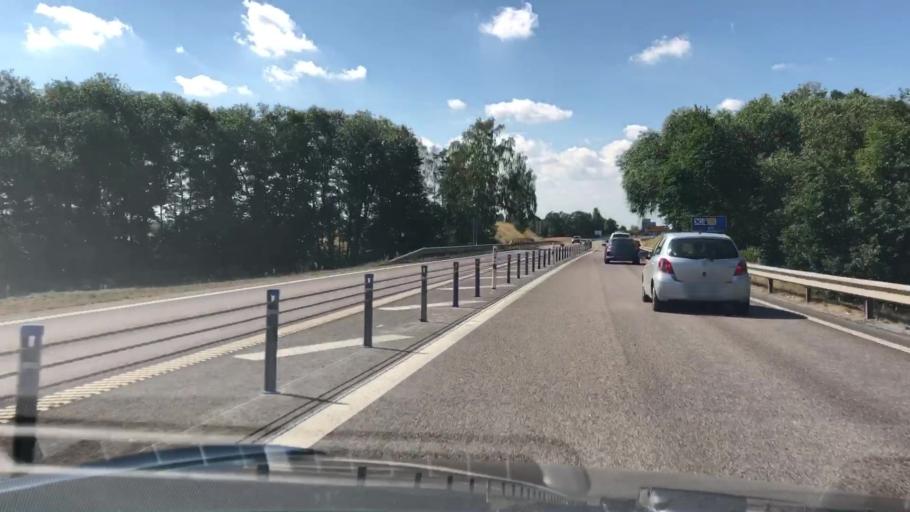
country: SE
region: Kalmar
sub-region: Kalmar Kommun
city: Lindsdal
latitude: 56.8043
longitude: 16.3641
